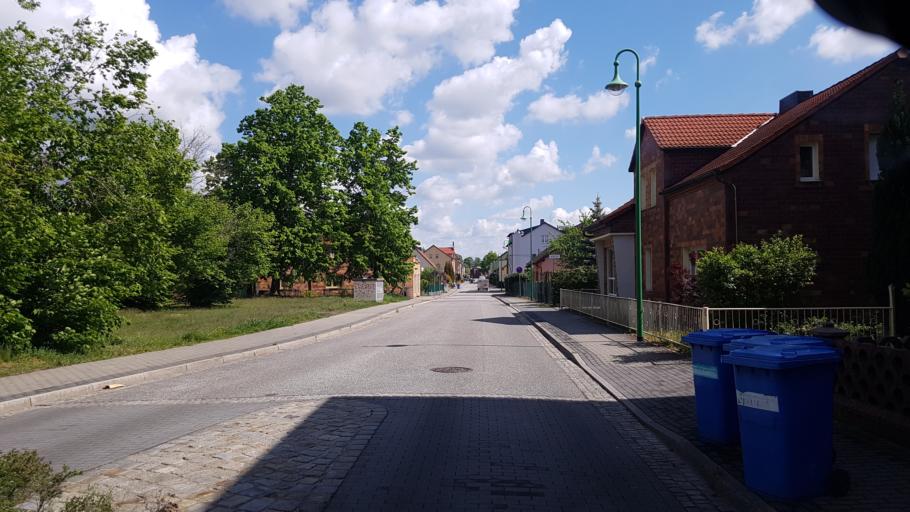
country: DE
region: Brandenburg
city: Grossraschen
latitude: 51.5810
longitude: 14.0014
